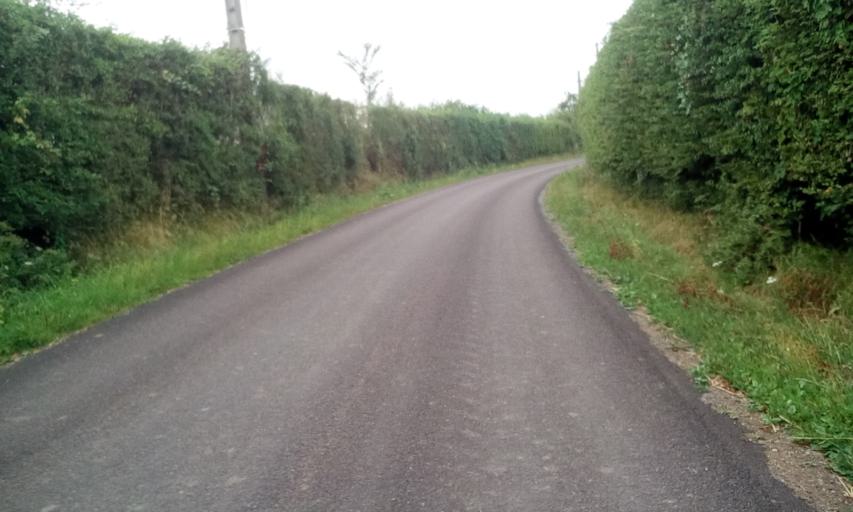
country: FR
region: Lower Normandy
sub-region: Departement du Calvados
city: Troarn
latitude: 49.1889
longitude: -0.1576
